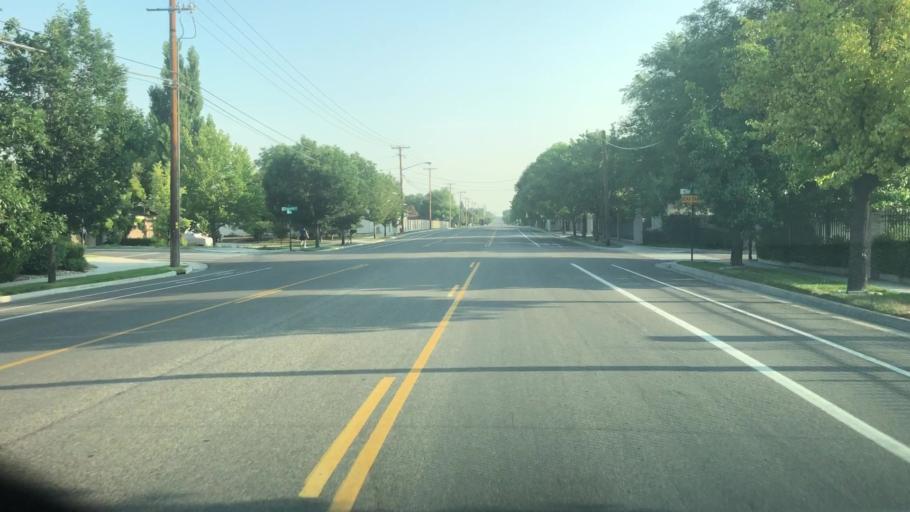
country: US
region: Utah
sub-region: Salt Lake County
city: South Jordan
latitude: 40.5458
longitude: -111.9291
